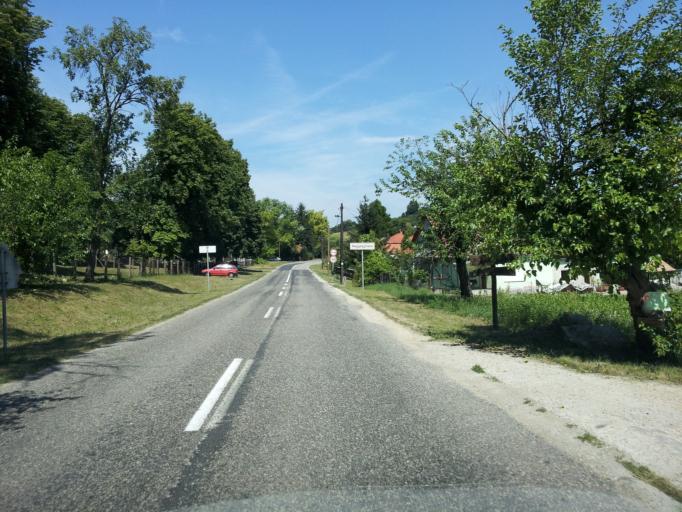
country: HU
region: Fejer
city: Szarliget
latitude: 47.5164
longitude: 18.5326
